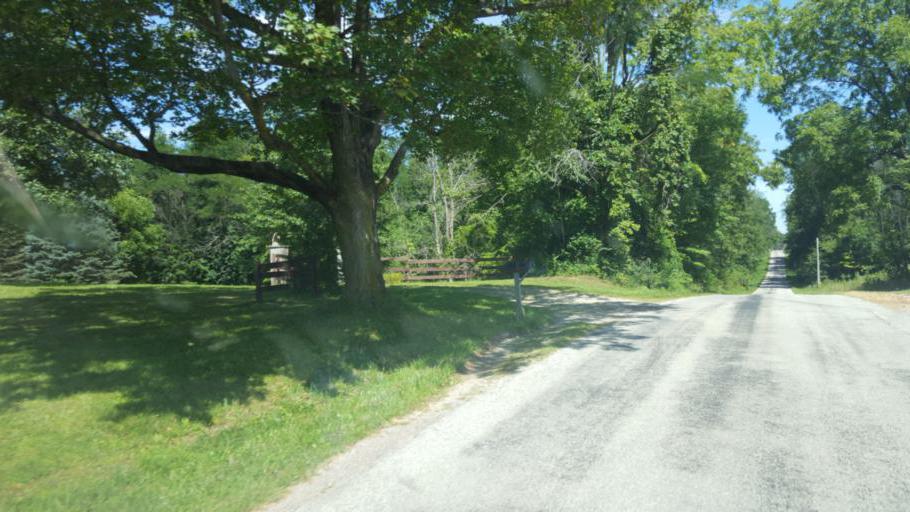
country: US
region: Ohio
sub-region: Knox County
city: Centerburg
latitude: 40.4152
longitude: -82.7681
